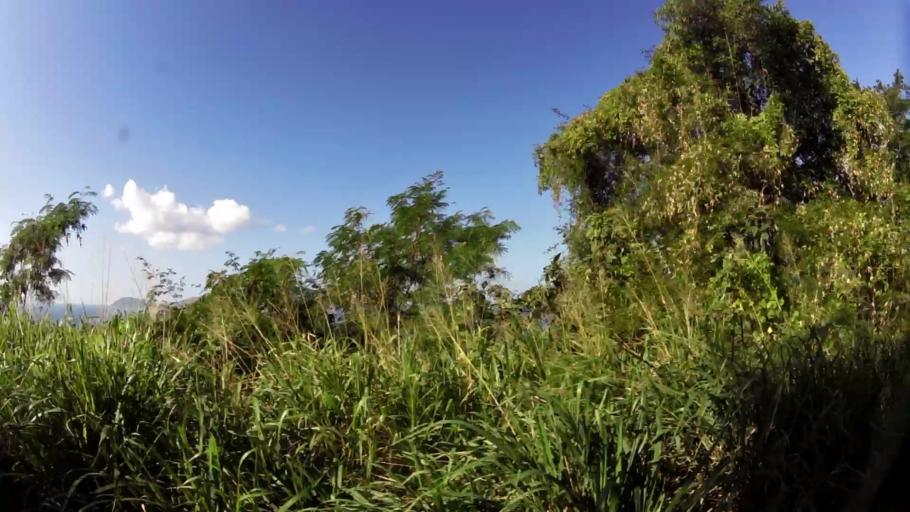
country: VG
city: Road Town
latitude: 18.3910
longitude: -64.7090
